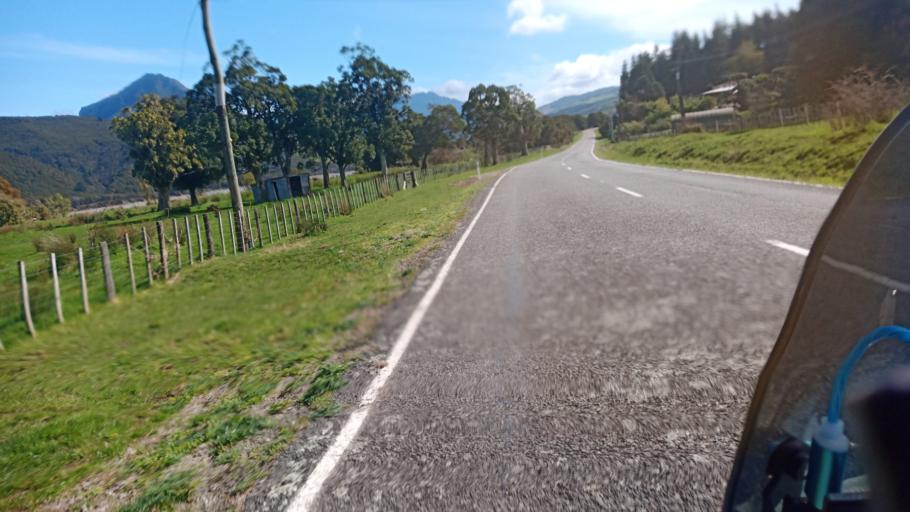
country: NZ
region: Gisborne
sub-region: Gisborne District
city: Gisborne
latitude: -37.8627
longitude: 178.1751
